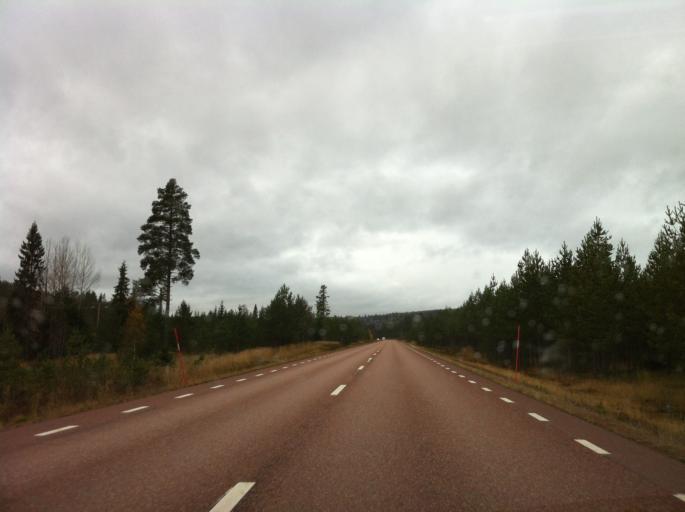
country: SE
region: Dalarna
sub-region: Alvdalens Kommun
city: AElvdalen
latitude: 61.2777
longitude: 13.8821
